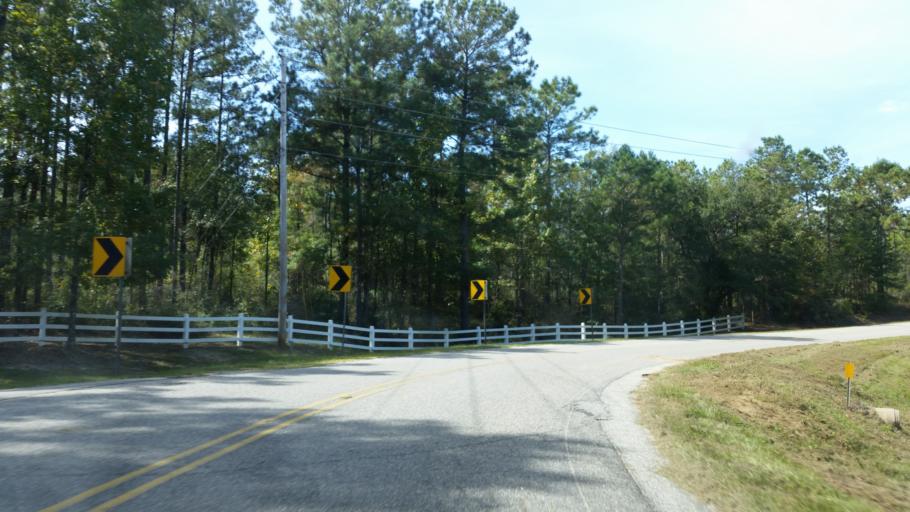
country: US
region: Alabama
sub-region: Baldwin County
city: Spanish Fort
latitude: 30.7396
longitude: -87.8829
